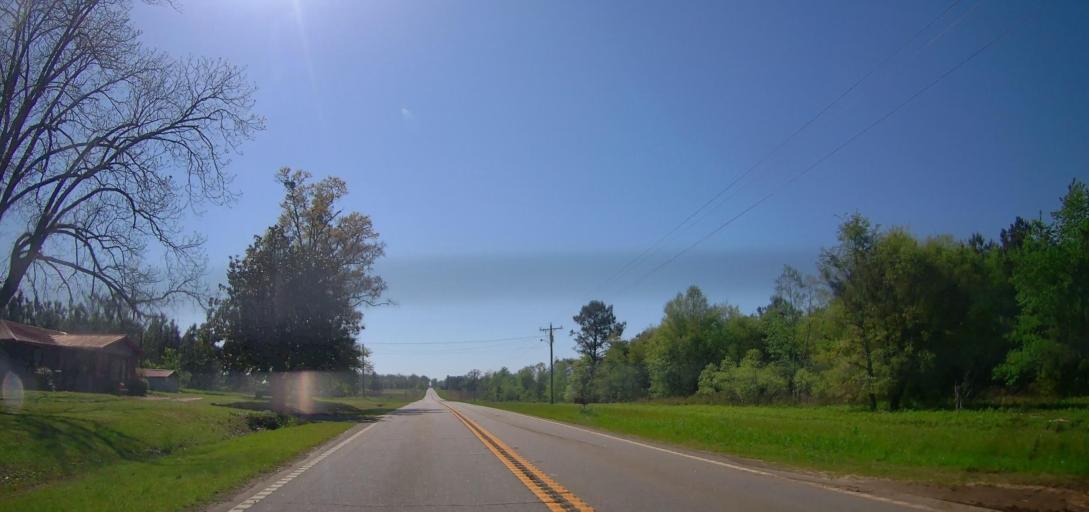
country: US
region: Georgia
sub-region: Dooly County
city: Unadilla
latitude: 32.2601
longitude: -83.6909
